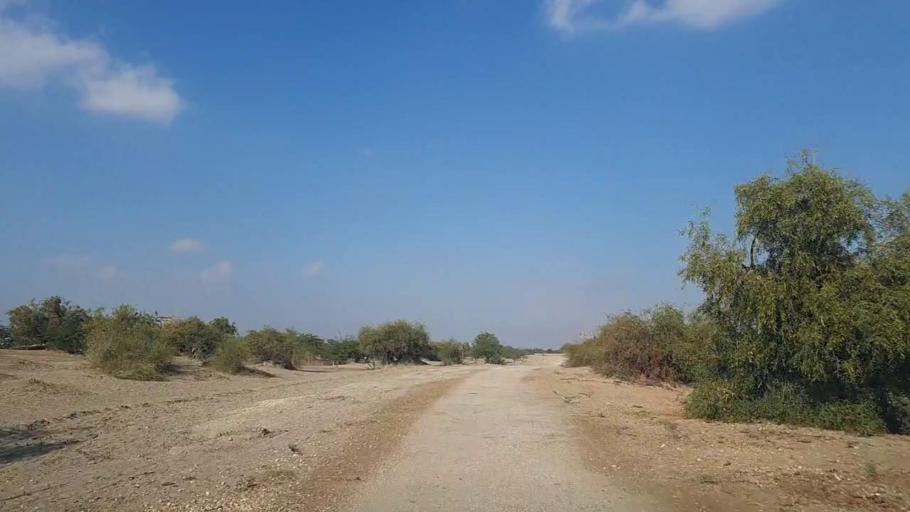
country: PK
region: Sindh
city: Tando Mittha Khan
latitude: 26.0167
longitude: 69.2496
